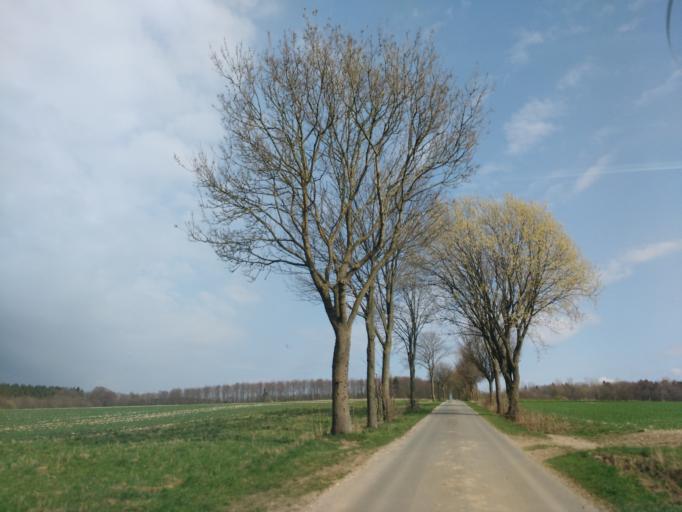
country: DE
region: North Rhine-Westphalia
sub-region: Regierungsbezirk Detmold
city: Schlangen
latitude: 51.7608
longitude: 8.8725
